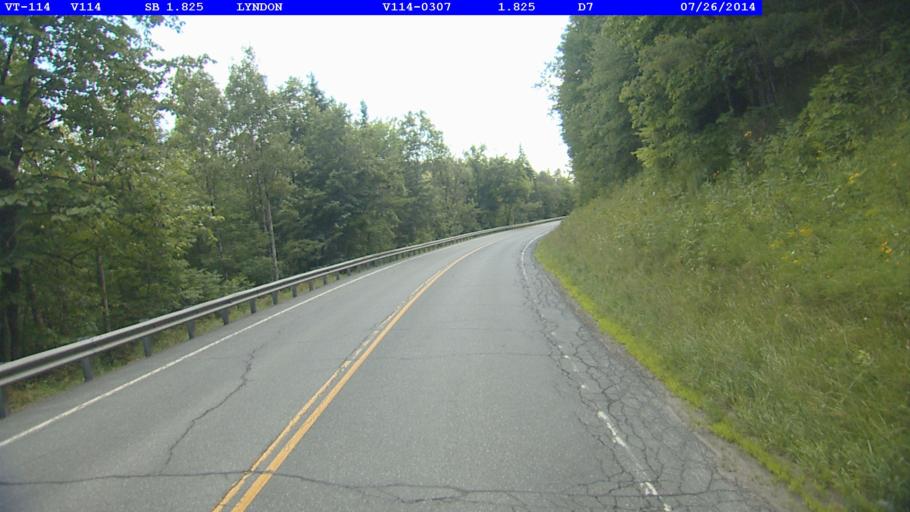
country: US
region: Vermont
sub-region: Caledonia County
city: Lyndonville
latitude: 44.5552
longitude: -71.9675
